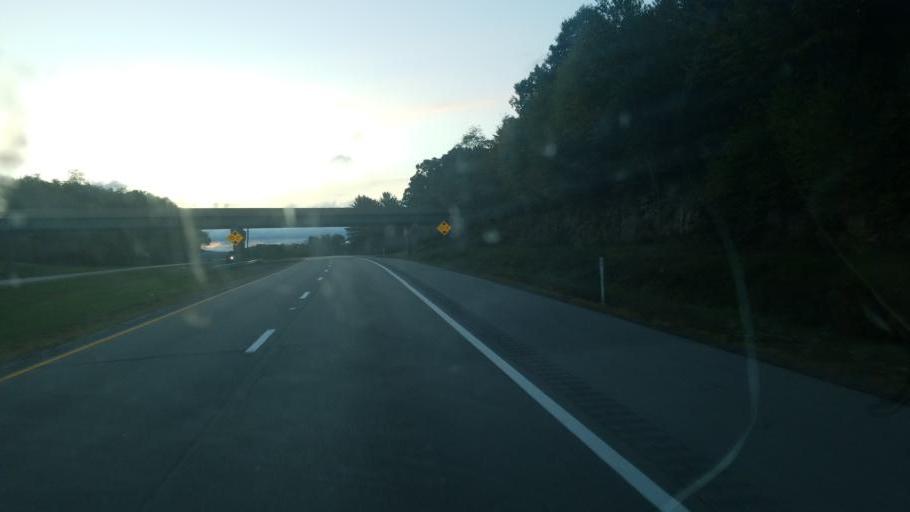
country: US
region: West Virginia
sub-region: Preston County
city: Terra Alta
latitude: 39.6579
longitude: -79.5750
